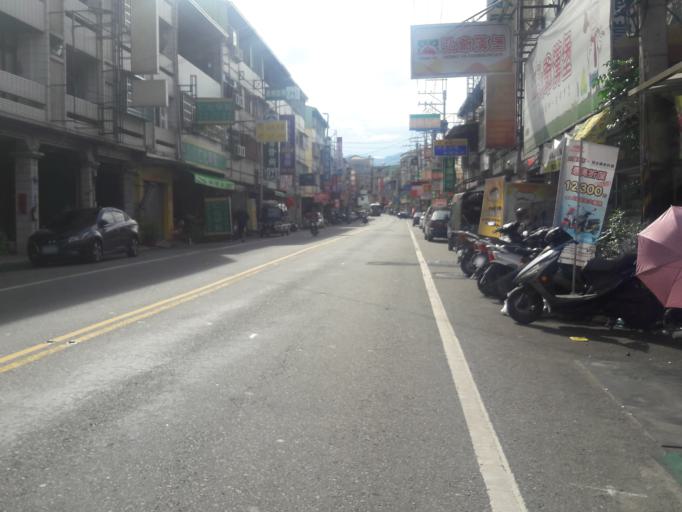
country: TW
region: Taiwan
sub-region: Taichung City
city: Taichung
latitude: 24.0964
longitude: 120.6998
